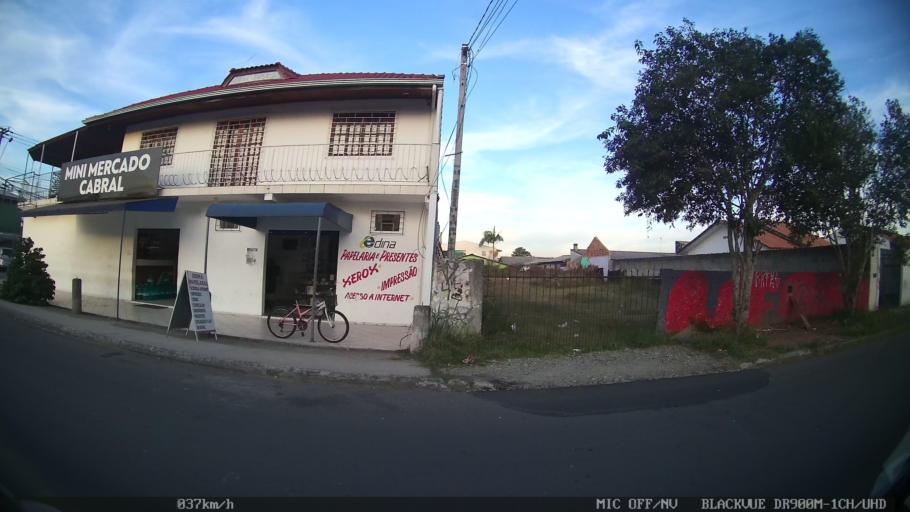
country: BR
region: Parana
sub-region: Pinhais
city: Pinhais
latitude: -25.4436
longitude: -49.1814
